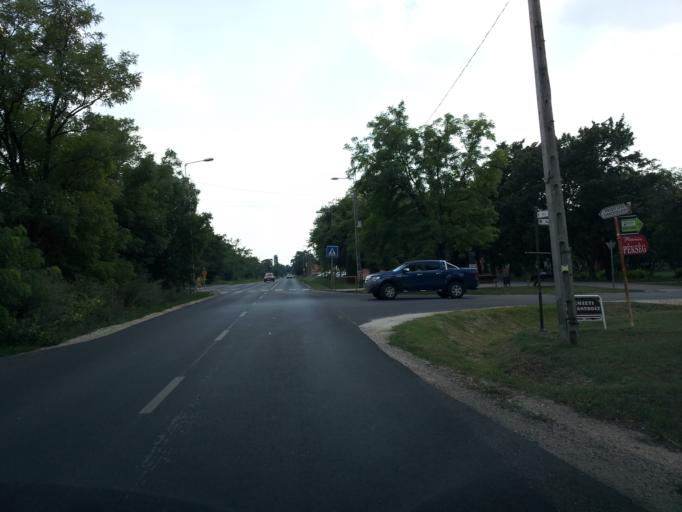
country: HU
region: Pest
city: Toekoel
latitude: 47.3387
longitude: 18.9697
